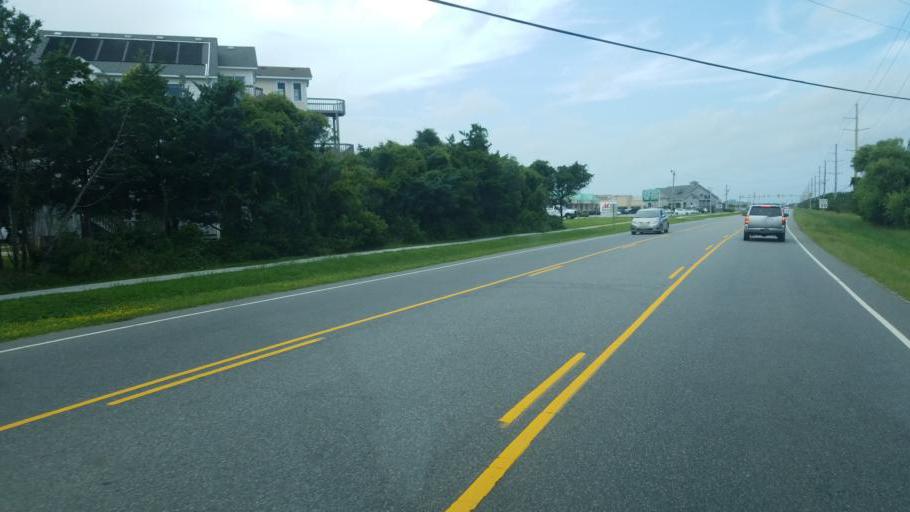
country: US
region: North Carolina
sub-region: Dare County
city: Buxton
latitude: 35.3308
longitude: -75.5075
